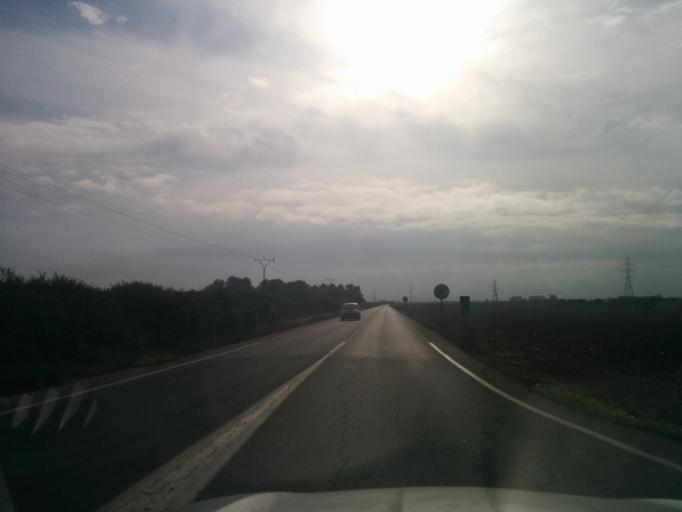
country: ES
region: Andalusia
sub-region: Provincia de Sevilla
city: La Algaba
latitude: 37.4528
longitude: -5.9990
